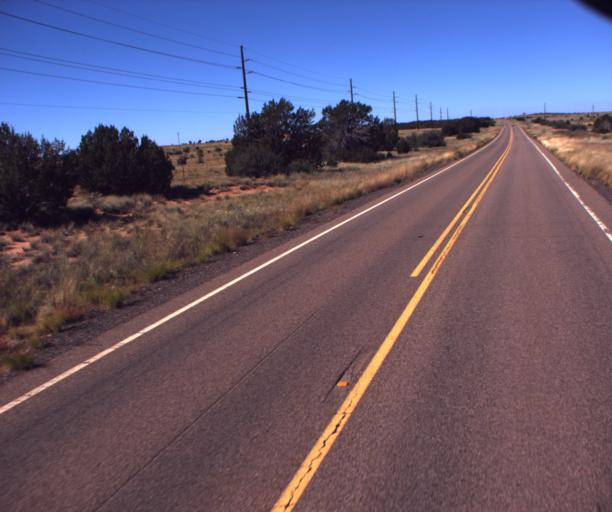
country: US
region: Arizona
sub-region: Navajo County
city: Taylor
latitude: 34.4831
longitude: -110.3196
